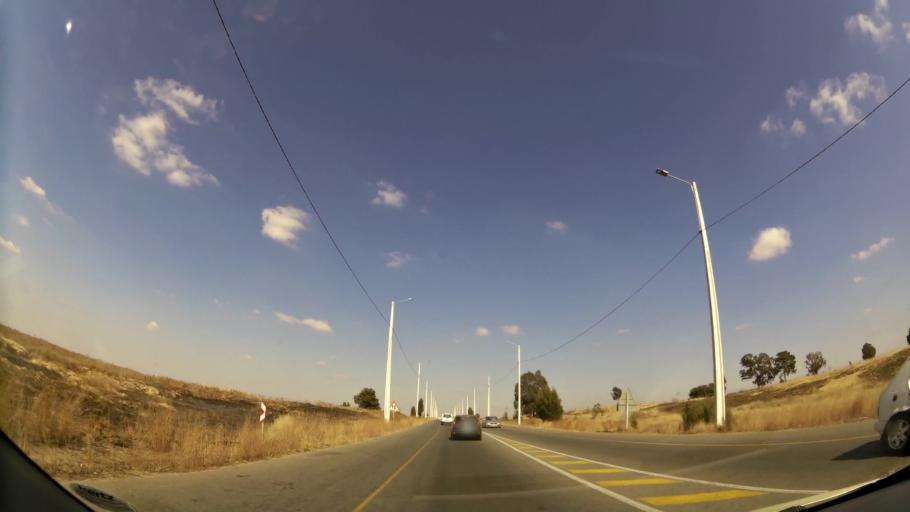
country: ZA
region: Gauteng
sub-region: West Rand District Municipality
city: Randfontein
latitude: -26.1578
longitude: 27.7622
